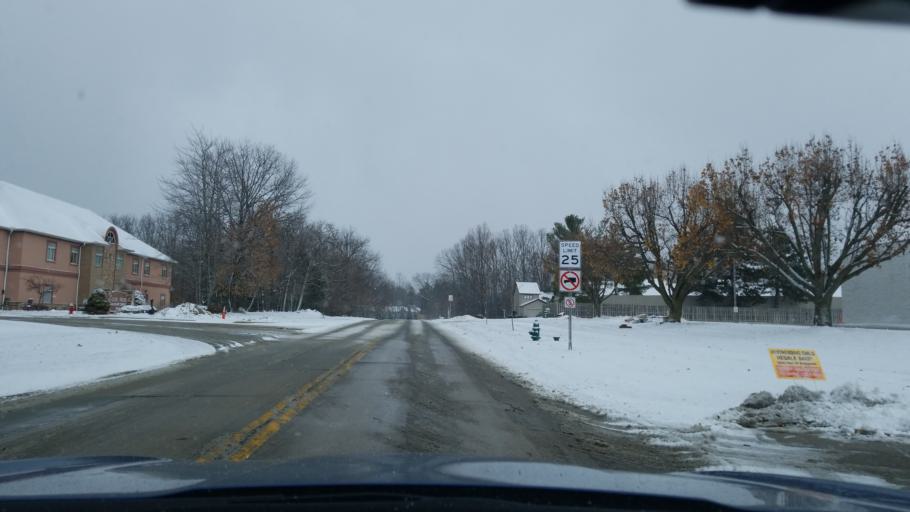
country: US
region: Ohio
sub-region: Cuyahoga County
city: Strongsville
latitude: 41.3238
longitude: -81.8352
